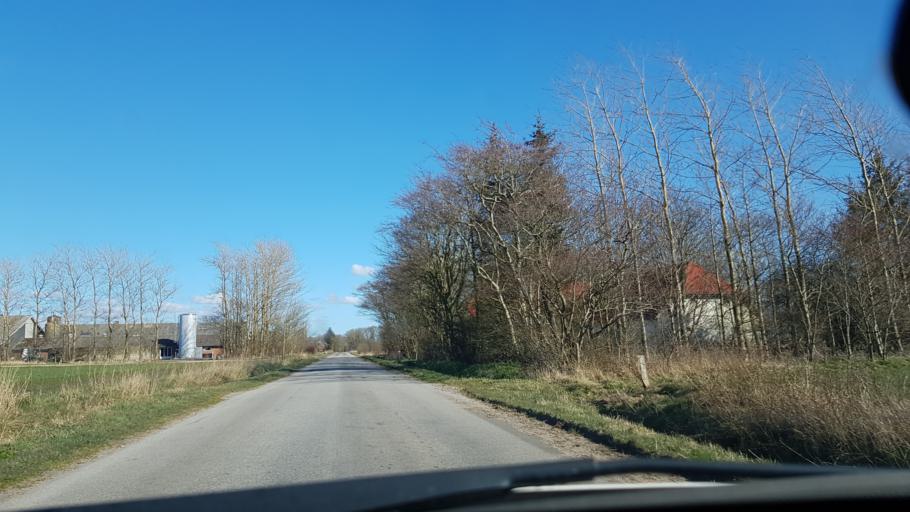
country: DK
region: South Denmark
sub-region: Tonder Kommune
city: Sherrebek
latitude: 55.2286
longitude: 8.7857
